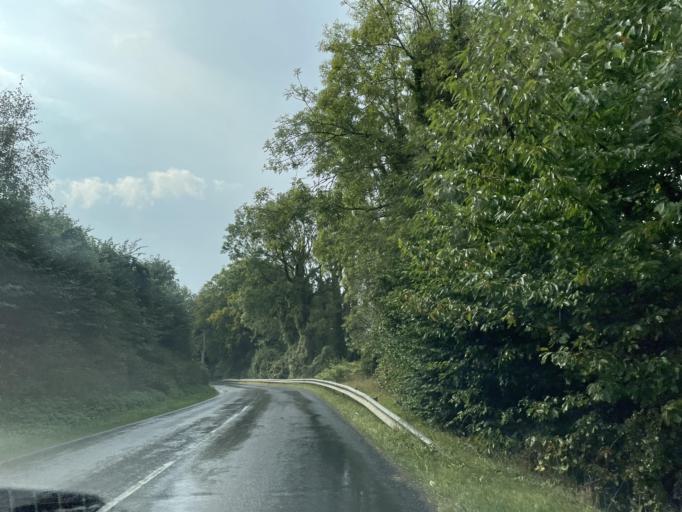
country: FR
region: Haute-Normandie
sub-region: Departement de la Seine-Maritime
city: Envermeu
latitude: 49.9078
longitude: 1.2721
